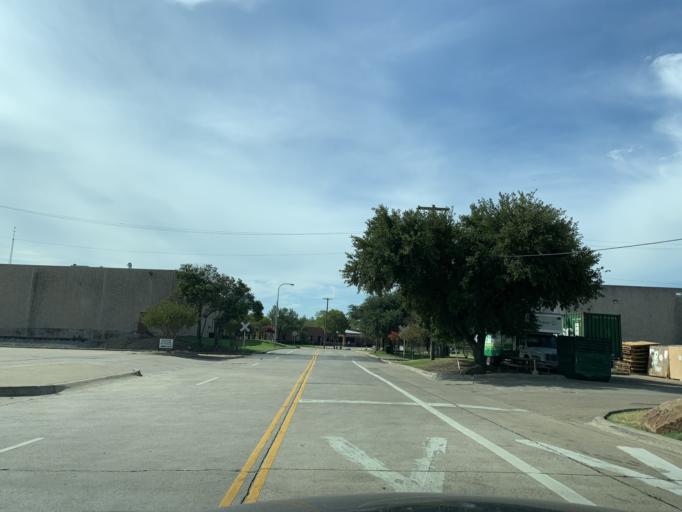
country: US
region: Texas
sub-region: Dallas County
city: Cockrell Hill
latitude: 32.7708
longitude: -96.8808
